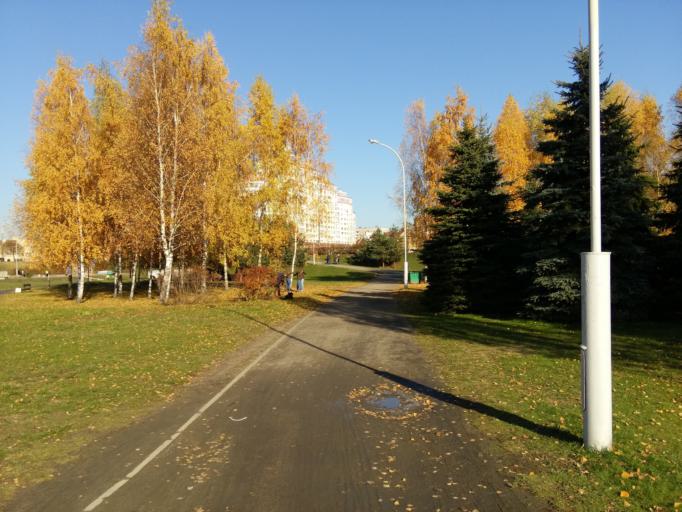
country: BY
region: Minsk
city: Borovlyany
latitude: 53.9458
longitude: 27.6798
